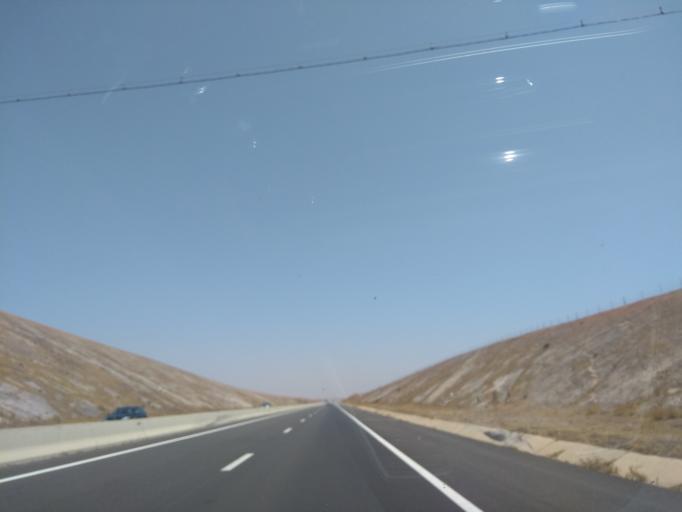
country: MA
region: Marrakech-Tensift-Al Haouz
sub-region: Kelaa-Des-Sraghna
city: Sidi Abdallah
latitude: 32.3095
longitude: -7.9589
